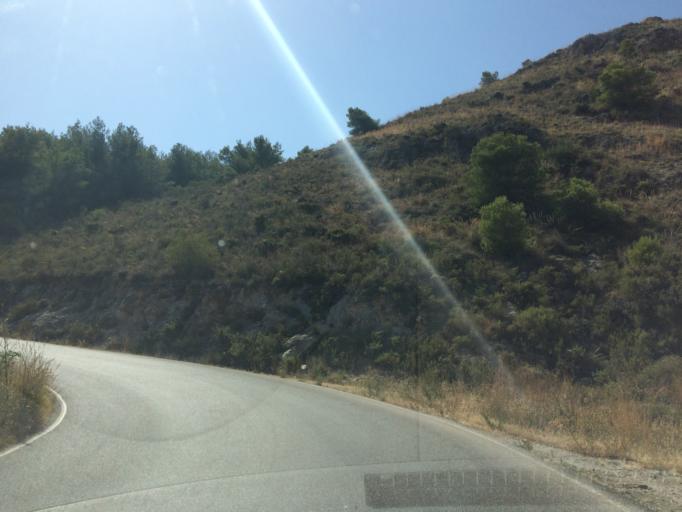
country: ES
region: Andalusia
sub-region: Provincia de Malaga
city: Frigiliana
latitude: 36.7980
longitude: -3.9023
